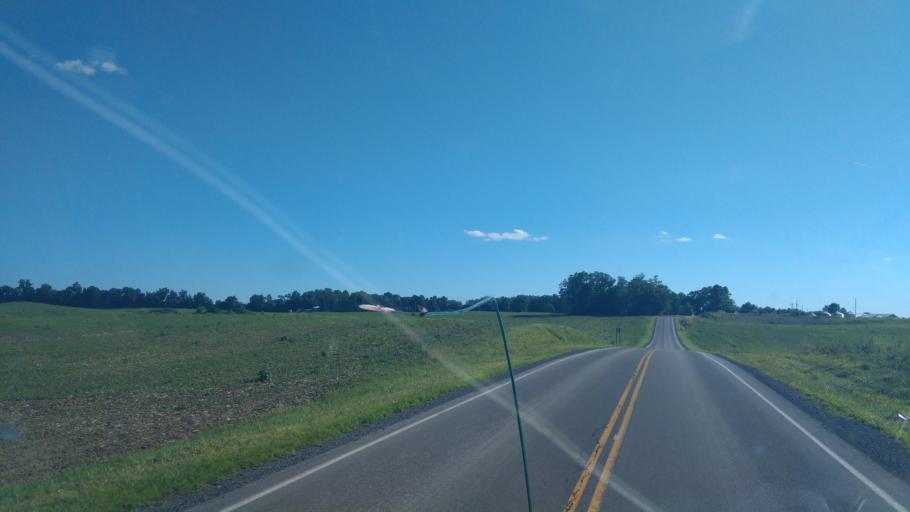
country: US
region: New York
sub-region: Wayne County
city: Clyde
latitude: 42.9994
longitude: -76.9044
